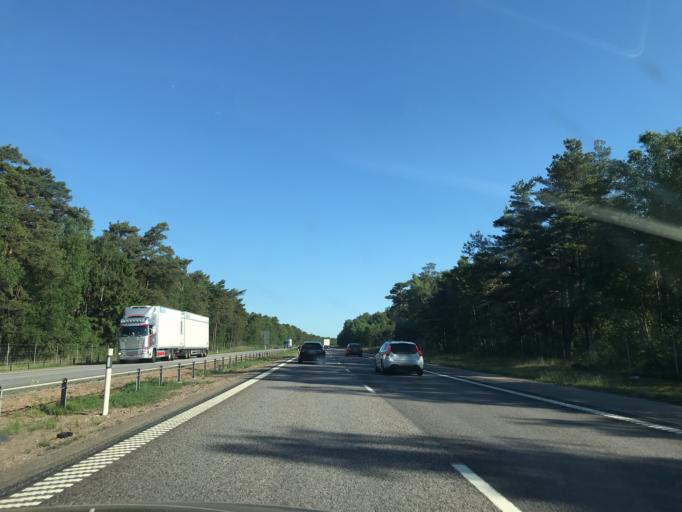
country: SE
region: Halland
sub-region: Halmstads Kommun
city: Paarp
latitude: 56.5592
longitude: 12.9572
